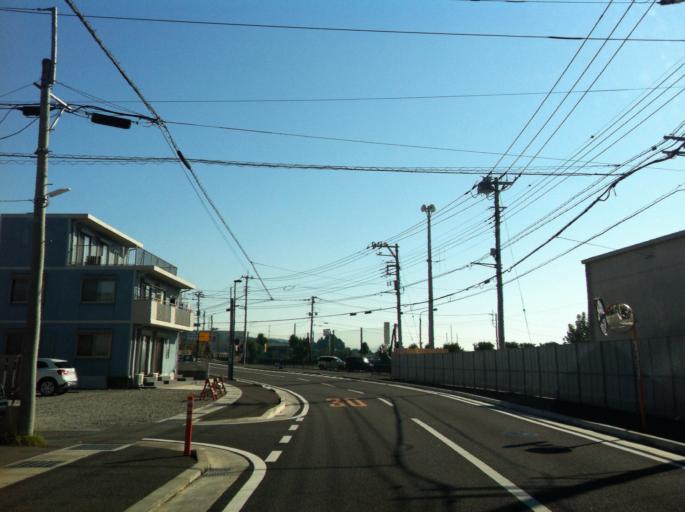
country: JP
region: Shizuoka
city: Fuji
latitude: 35.1629
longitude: 138.7377
